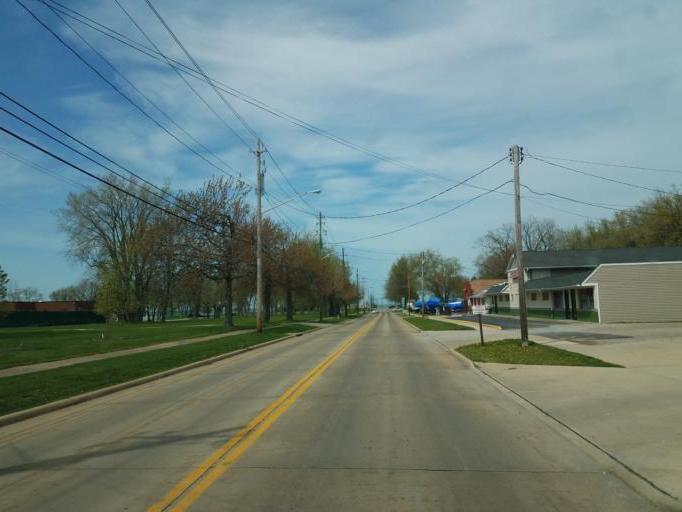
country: US
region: Ohio
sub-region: Lake County
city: Mentor-on-the-Lake
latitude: 41.7178
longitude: -81.3614
